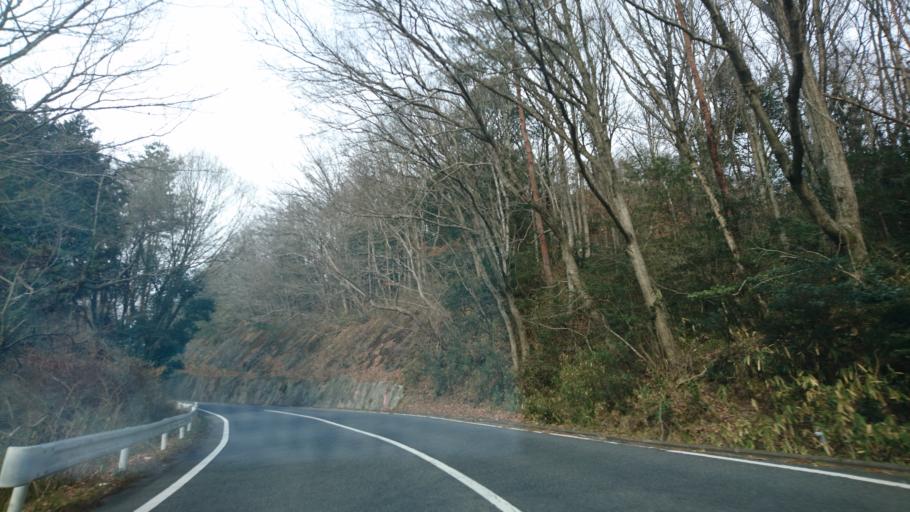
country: JP
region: Okayama
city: Takahashi
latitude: 34.8254
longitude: 133.6680
